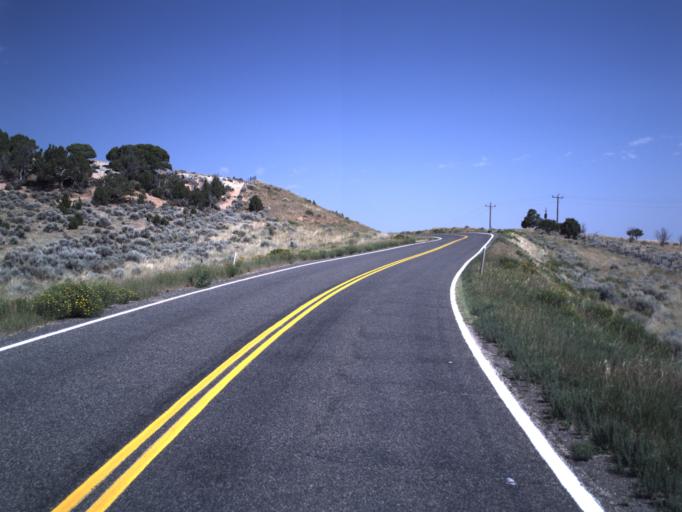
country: US
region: Utah
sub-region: Daggett County
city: Manila
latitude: 40.9800
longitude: -109.8375
